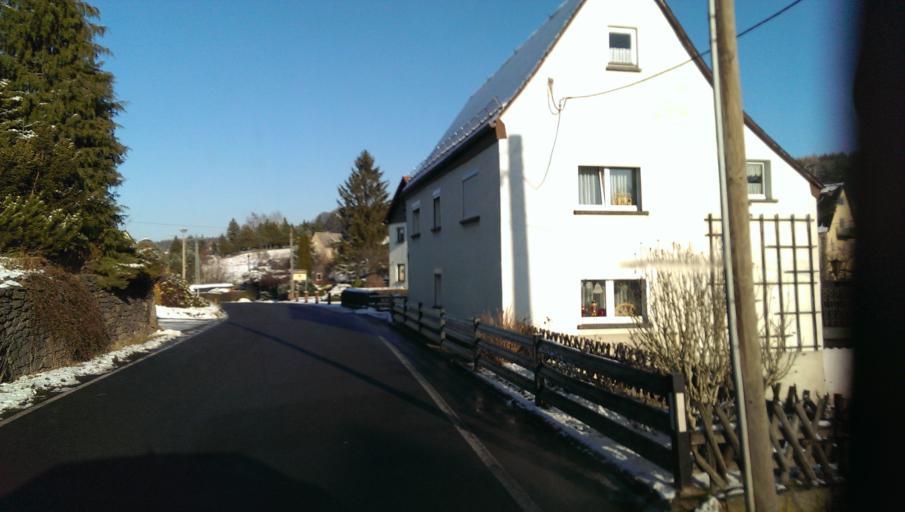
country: DE
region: Saxony
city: Dorfhain
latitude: 50.9178
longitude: 13.5898
